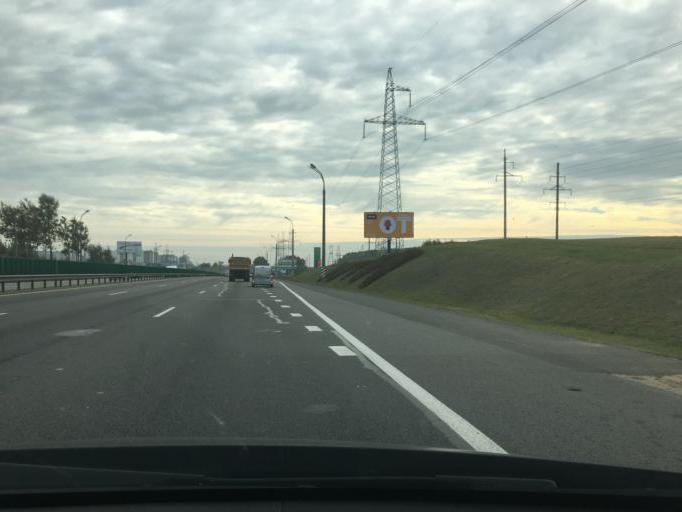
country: BY
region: Minsk
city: Malinovka
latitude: 53.8737
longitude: 27.4205
